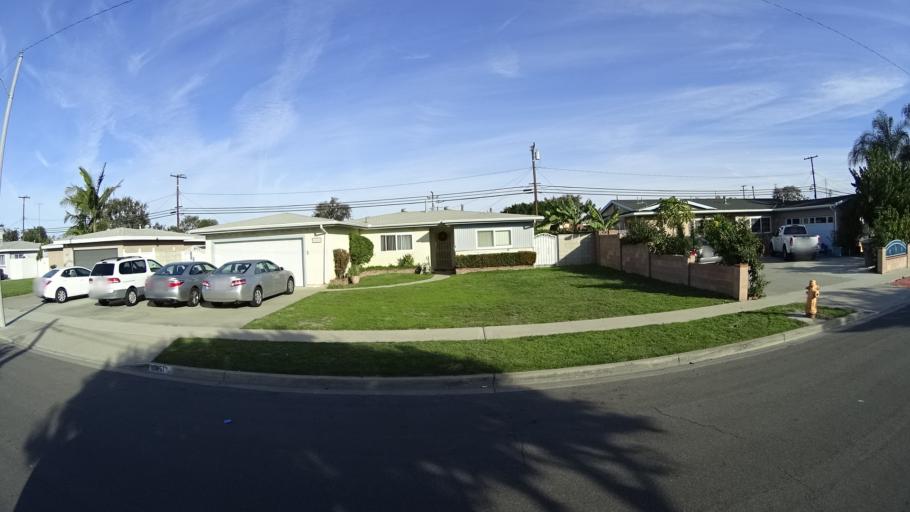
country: US
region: California
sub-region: Orange County
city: Garden Grove
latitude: 33.7629
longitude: -117.9399
